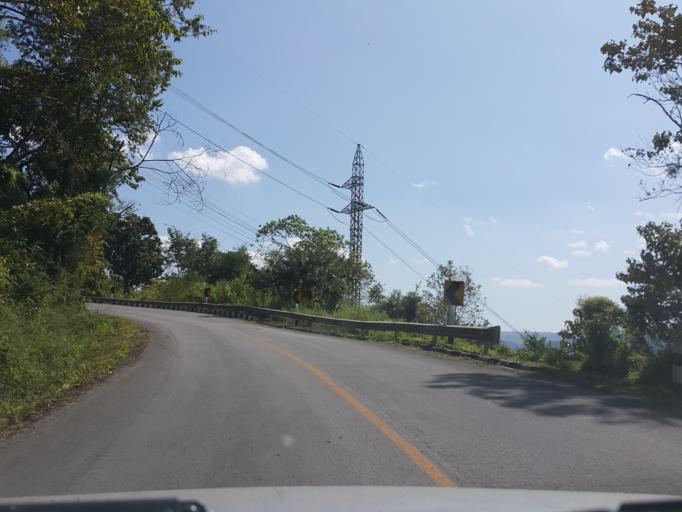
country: TH
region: Mae Hong Son
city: Mae Hi
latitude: 19.2241
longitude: 98.6721
